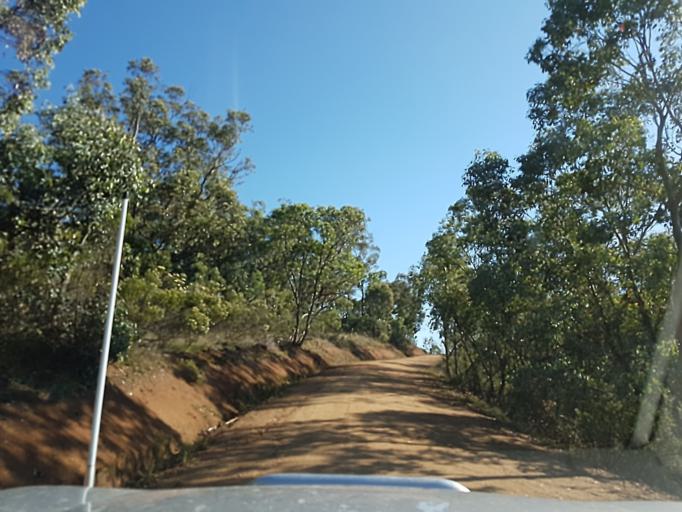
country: AU
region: New South Wales
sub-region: Snowy River
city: Jindabyne
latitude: -36.9462
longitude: 148.3470
